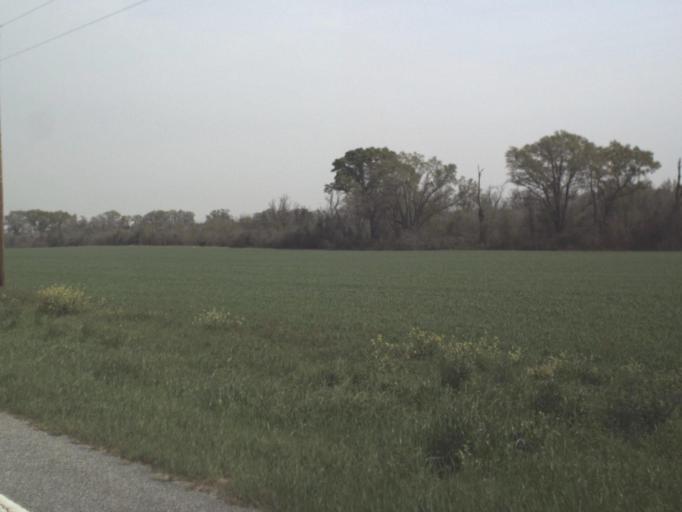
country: US
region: Florida
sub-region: Jackson County
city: Malone
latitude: 30.9758
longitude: -85.0482
